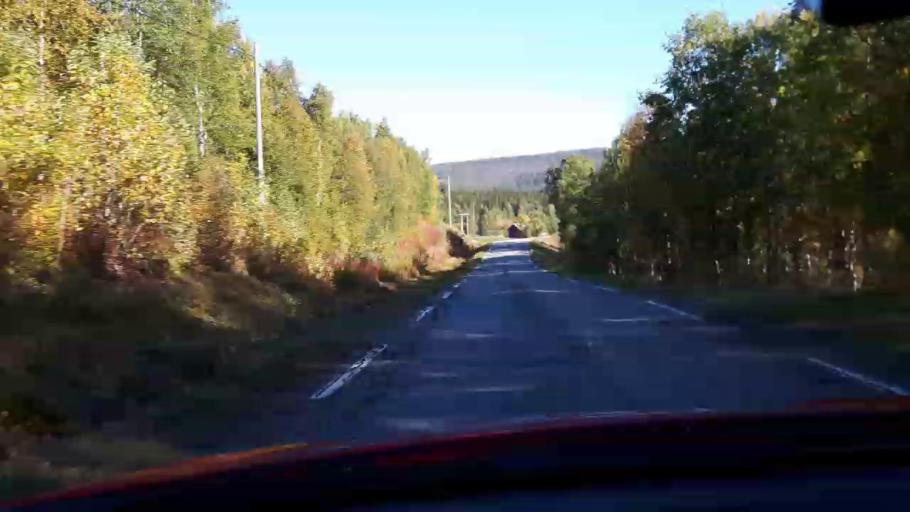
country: NO
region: Nord-Trondelag
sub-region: Lierne
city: Sandvika
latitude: 64.6335
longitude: 13.6951
